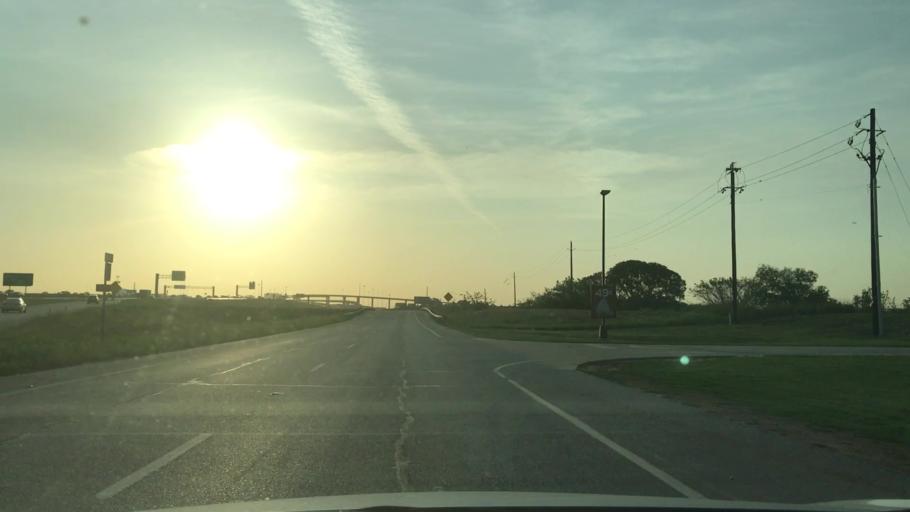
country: US
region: Texas
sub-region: Dallas County
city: Farmers Branch
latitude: 32.9059
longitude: -96.9177
